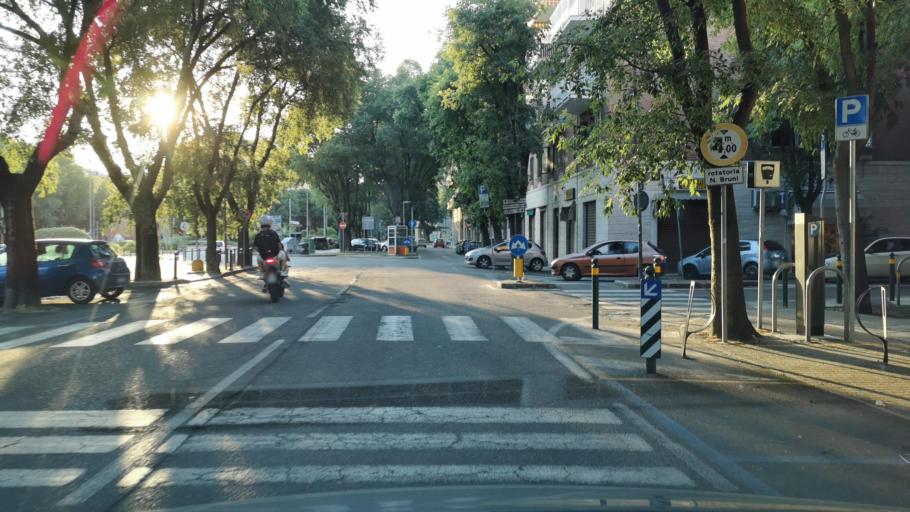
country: IT
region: Emilia-Romagna
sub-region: Provincia di Modena
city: Modena
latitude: 44.6516
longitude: 10.9344
